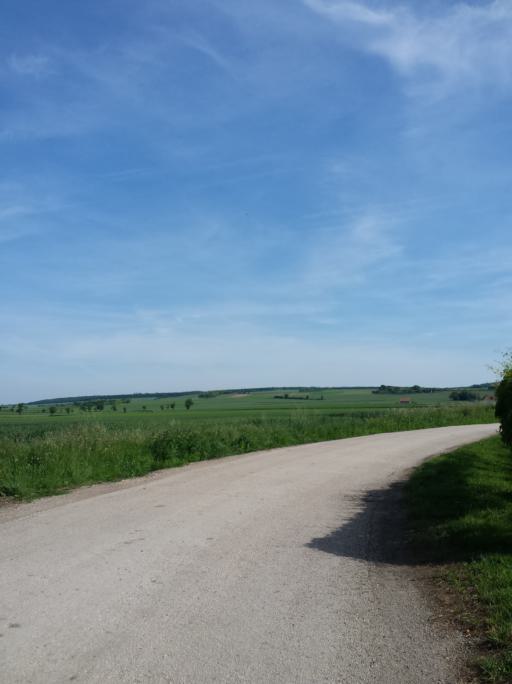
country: AT
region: Lower Austria
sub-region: Politischer Bezirk Hollabrunn
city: Wullersdorf
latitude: 48.6397
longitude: 16.1220
